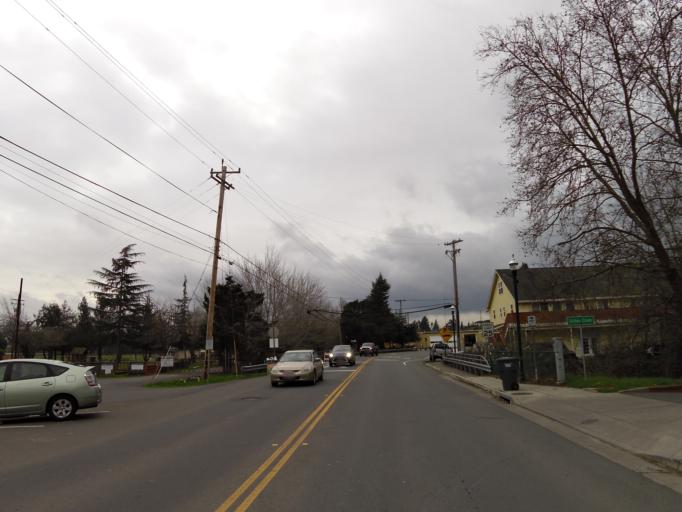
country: US
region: California
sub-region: Sonoma County
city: Penngrove
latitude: 38.2966
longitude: -122.6665
